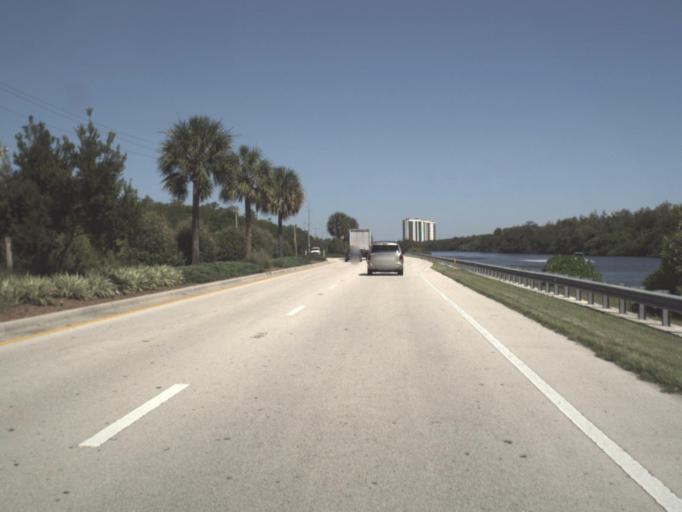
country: US
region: Florida
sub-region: Collier County
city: Marco
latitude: 25.9736
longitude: -81.7063
